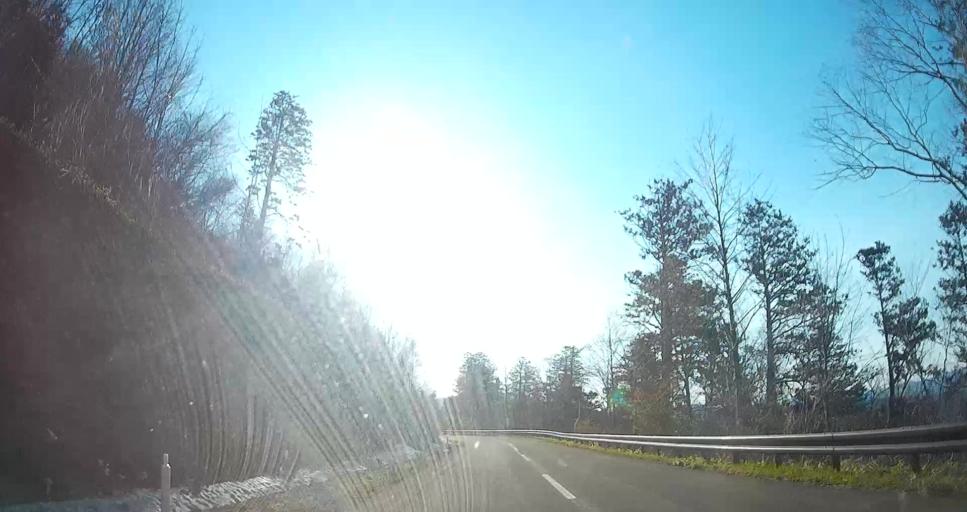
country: JP
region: Aomori
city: Mutsu
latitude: 41.3121
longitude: 141.1124
